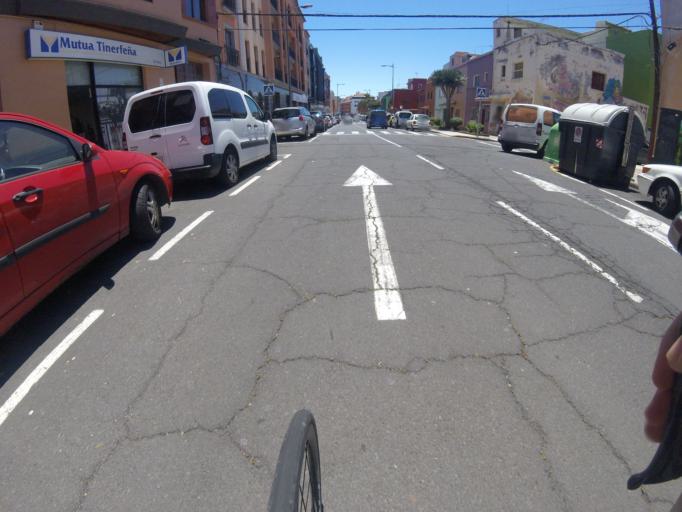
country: ES
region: Canary Islands
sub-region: Provincia de Santa Cruz de Tenerife
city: La Laguna
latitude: 28.4883
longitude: -16.3213
